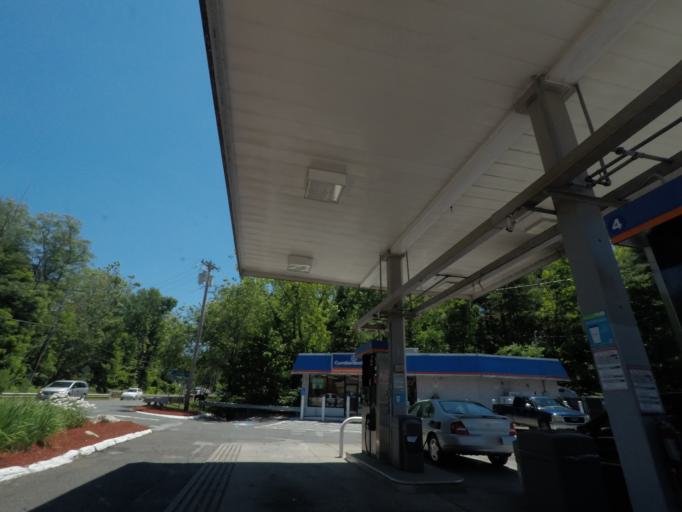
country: US
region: Massachusetts
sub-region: Hampden County
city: Granville
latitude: 42.1893
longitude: -72.8589
